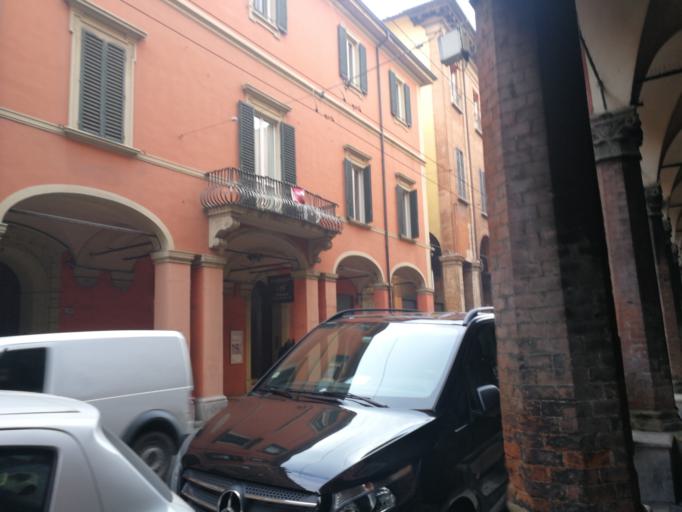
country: IT
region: Emilia-Romagna
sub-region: Provincia di Bologna
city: Bologna
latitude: 44.4963
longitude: 11.3356
